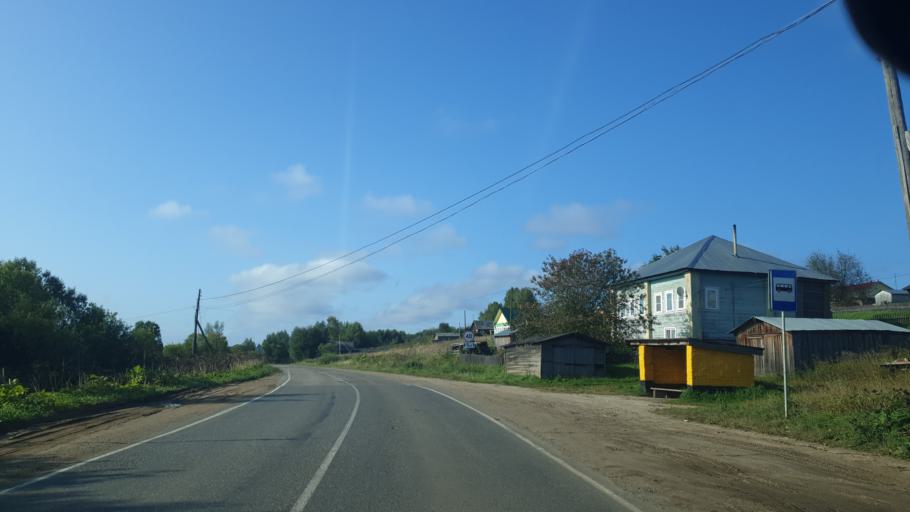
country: RU
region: Komi Republic
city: Vizinga
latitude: 60.9671
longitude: 50.2445
